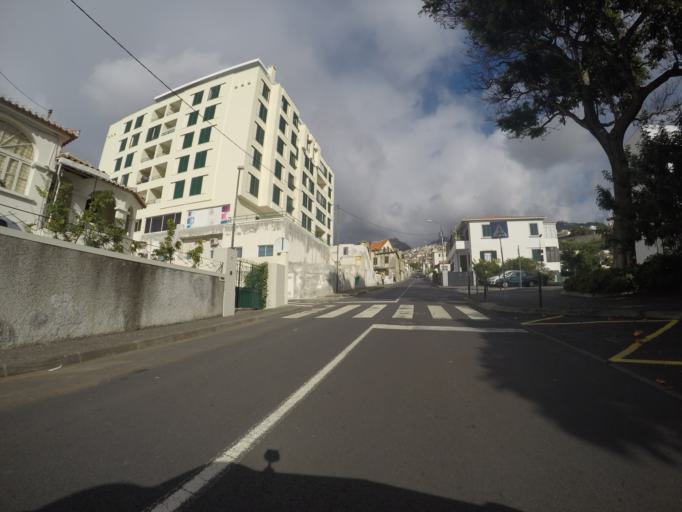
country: PT
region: Madeira
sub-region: Funchal
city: Nossa Senhora do Monte
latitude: 32.6551
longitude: -16.9125
